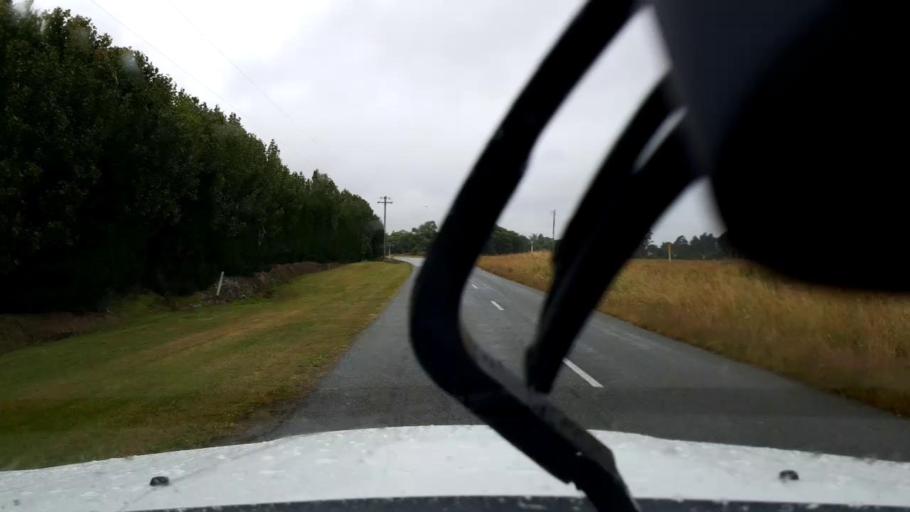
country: NZ
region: Canterbury
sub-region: Timaru District
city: Pleasant Point
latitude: -44.2532
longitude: 171.2519
